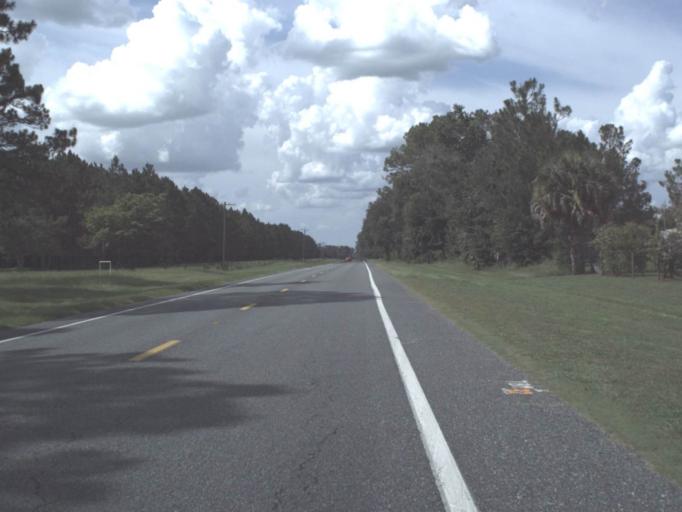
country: US
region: Florida
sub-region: Gilchrist County
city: Trenton
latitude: 29.5767
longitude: -82.8232
